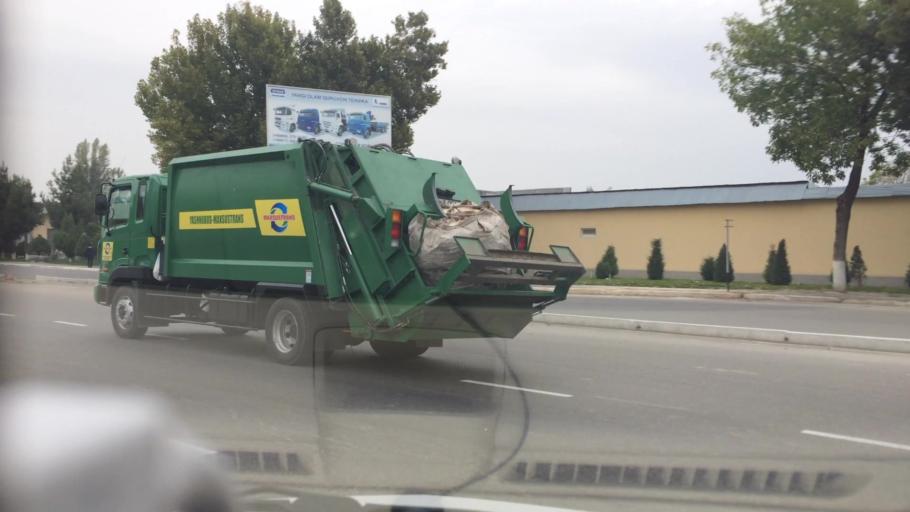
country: UZ
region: Toshkent
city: Salor
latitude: 41.3000
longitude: 69.3465
